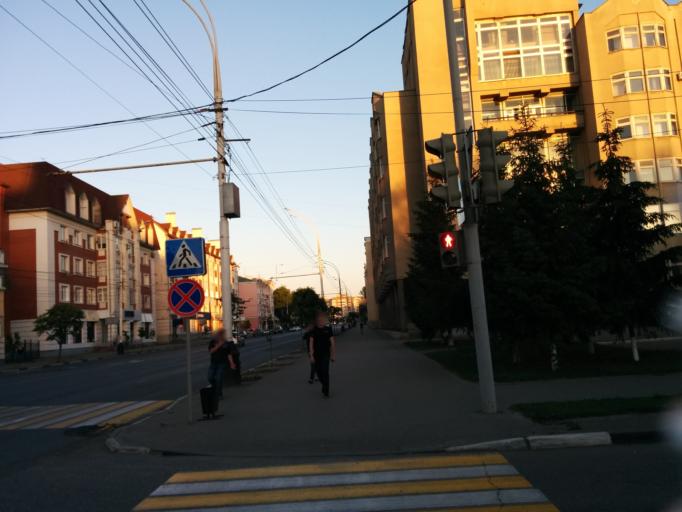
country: RU
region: Tambov
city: Tambov
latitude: 52.7101
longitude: 41.4650
